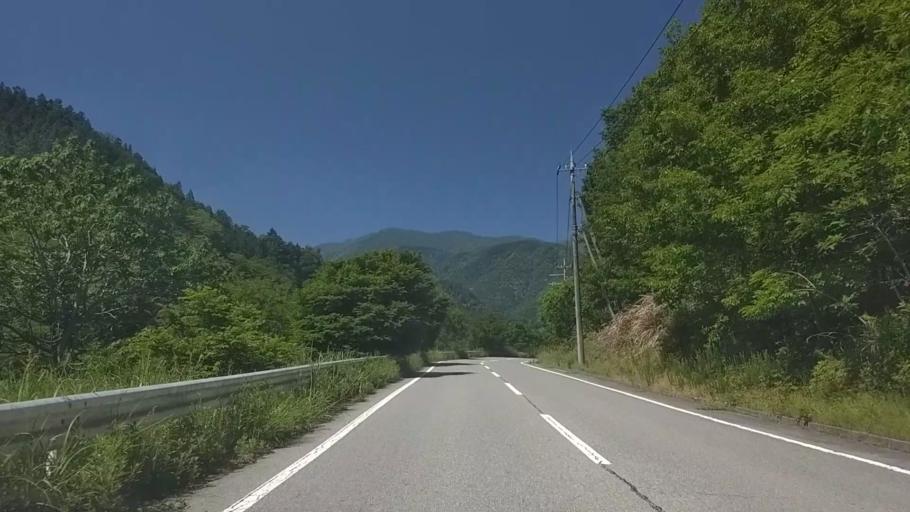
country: JP
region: Yamanashi
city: Ryuo
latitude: 35.5085
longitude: 138.4376
